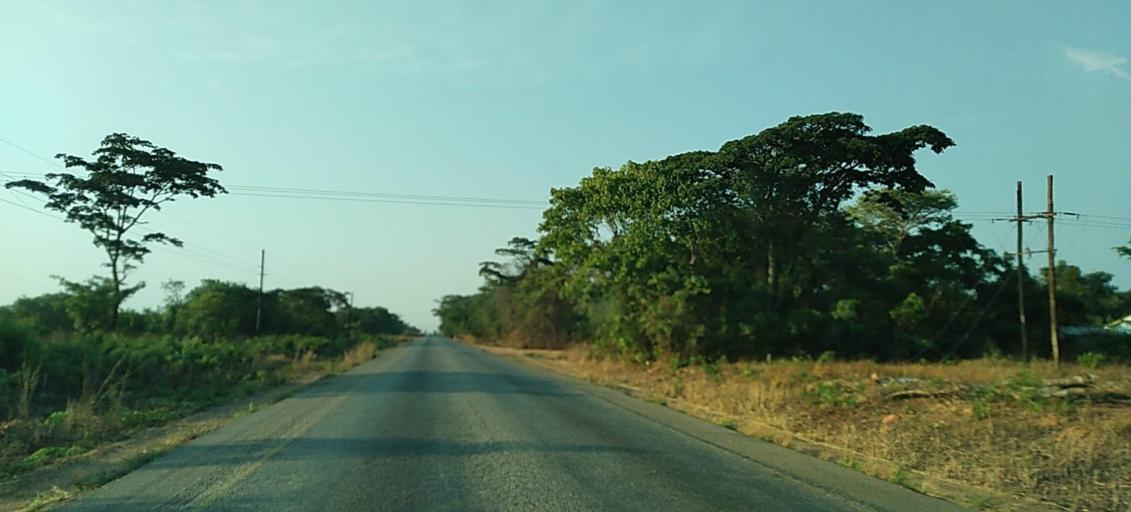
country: ZM
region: Copperbelt
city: Luanshya
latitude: -13.2361
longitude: 28.6790
